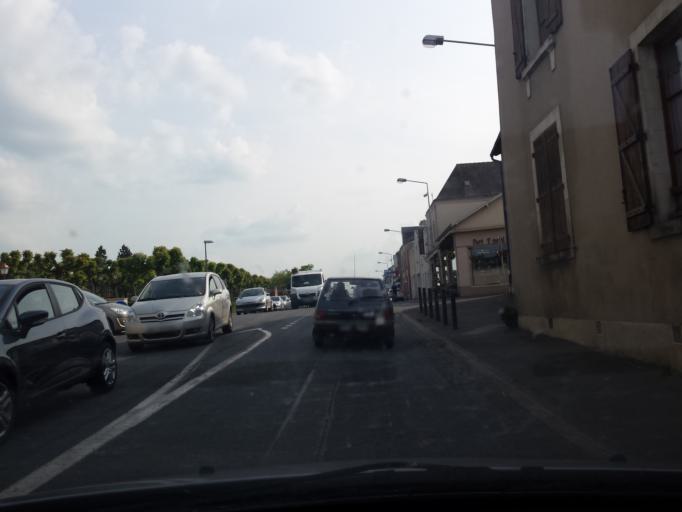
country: FR
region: Pays de la Loire
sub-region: Departement de Maine-et-Loire
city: Chemille-Melay
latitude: 47.2197
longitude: -0.7276
